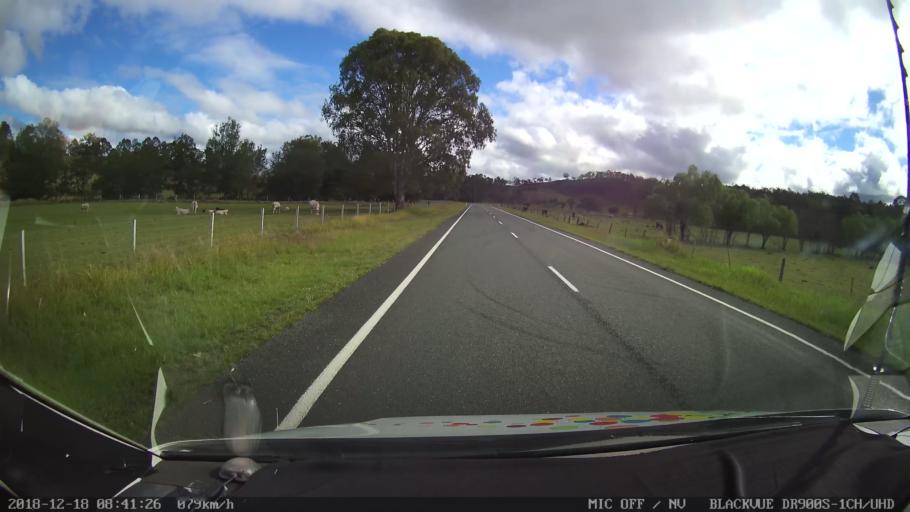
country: AU
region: Queensland
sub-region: Logan
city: Cedar Vale
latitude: -28.2364
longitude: 152.8570
